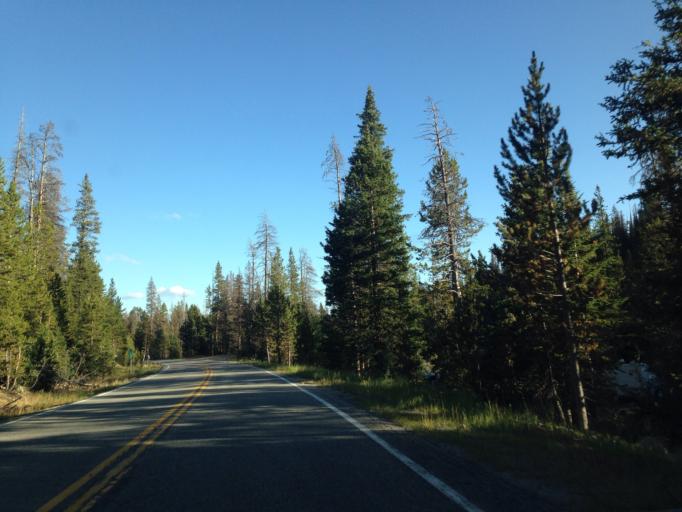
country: US
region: Utah
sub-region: Summit County
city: Kamas
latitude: 40.6723
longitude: -110.9509
